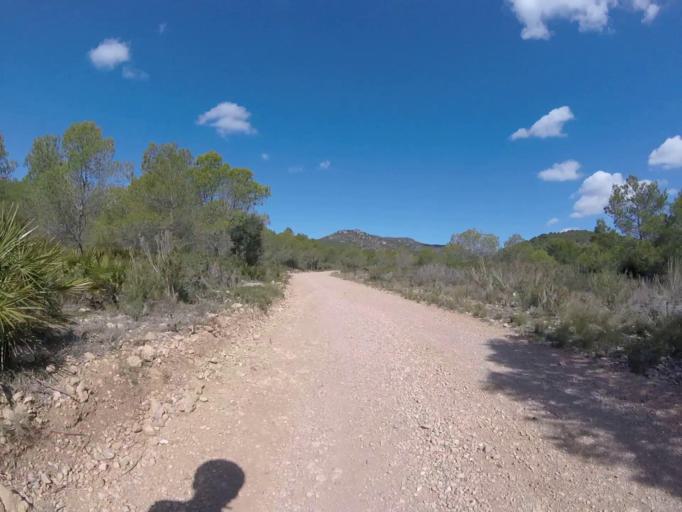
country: ES
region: Valencia
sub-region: Provincia de Castello
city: Alcoceber
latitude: 40.2880
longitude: 0.3188
